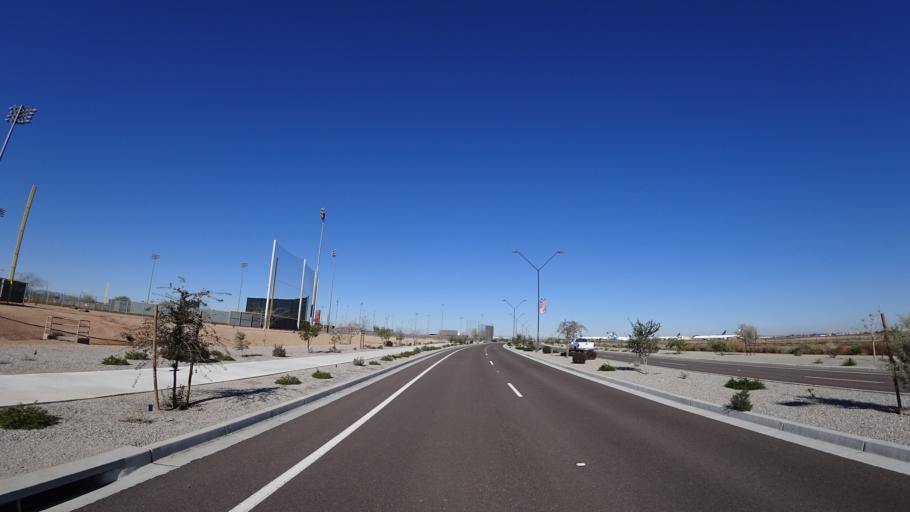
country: US
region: Arizona
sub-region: Maricopa County
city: Goodyear
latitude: 33.4175
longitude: -112.3868
